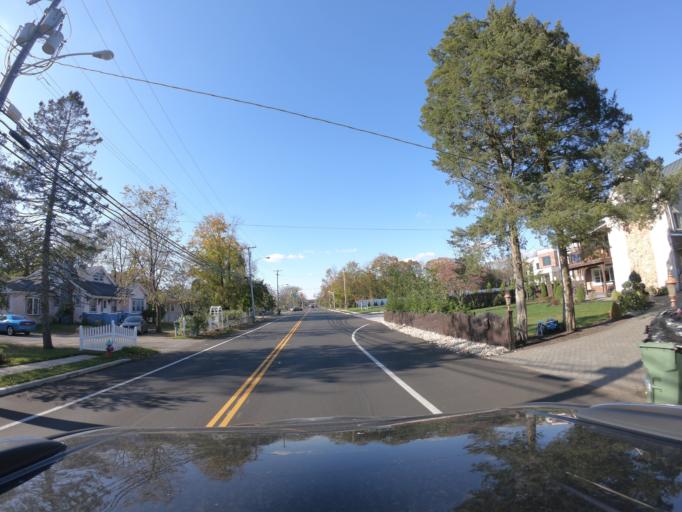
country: US
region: New Jersey
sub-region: Monmouth County
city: Ramtown
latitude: 40.1001
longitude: -74.1687
